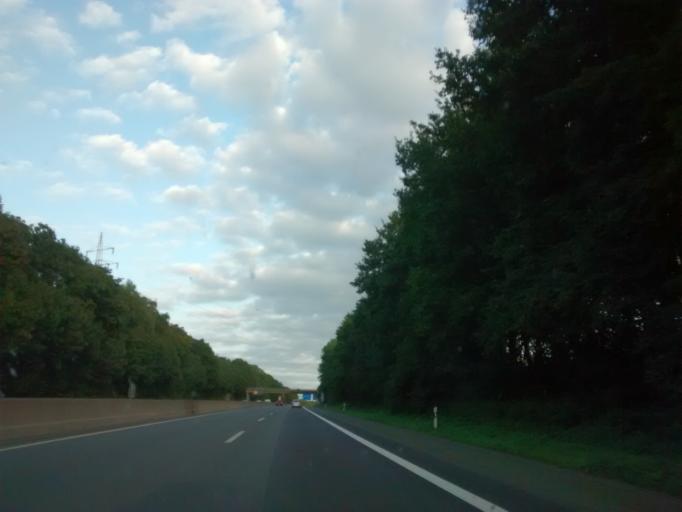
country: DE
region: North Rhine-Westphalia
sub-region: Regierungsbezirk Munster
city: Lotte
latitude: 52.2679
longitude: 7.9093
